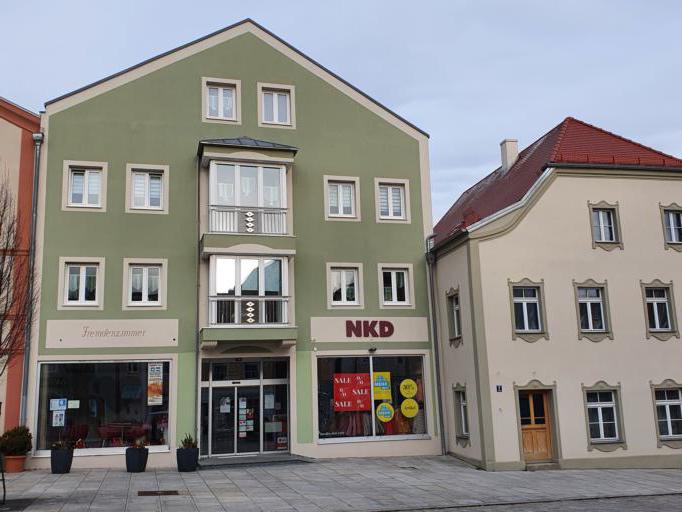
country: DE
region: Bavaria
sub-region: Upper Palatinate
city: Hemau
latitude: 49.0516
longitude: 11.7827
